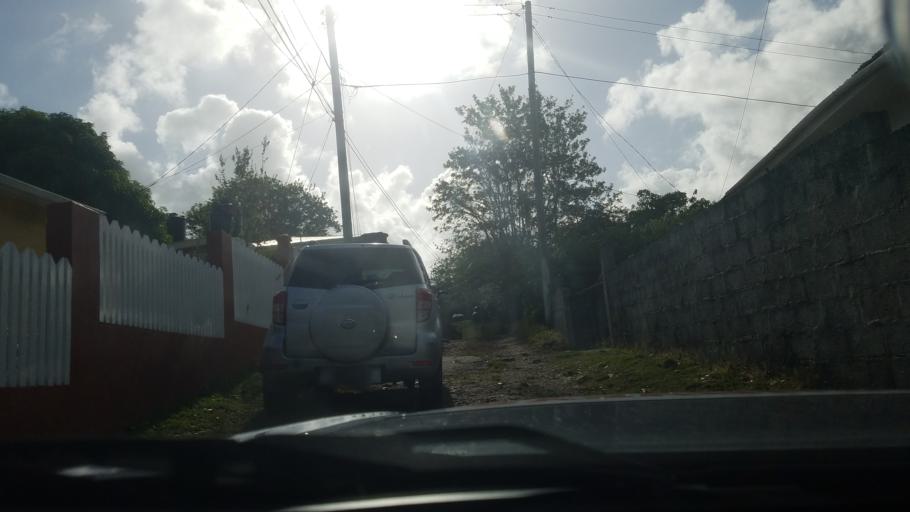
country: LC
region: Gros-Islet
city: Gros Islet
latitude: 14.0621
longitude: -60.9567
